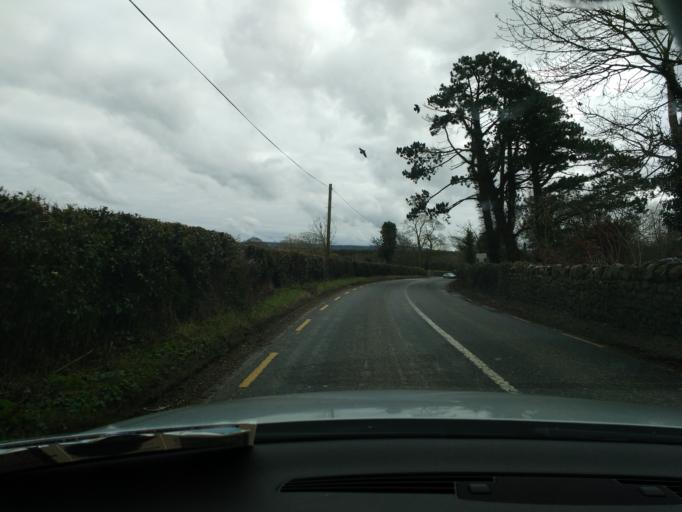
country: IE
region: Leinster
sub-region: Laois
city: Rathdowney
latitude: 52.7226
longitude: -7.5607
